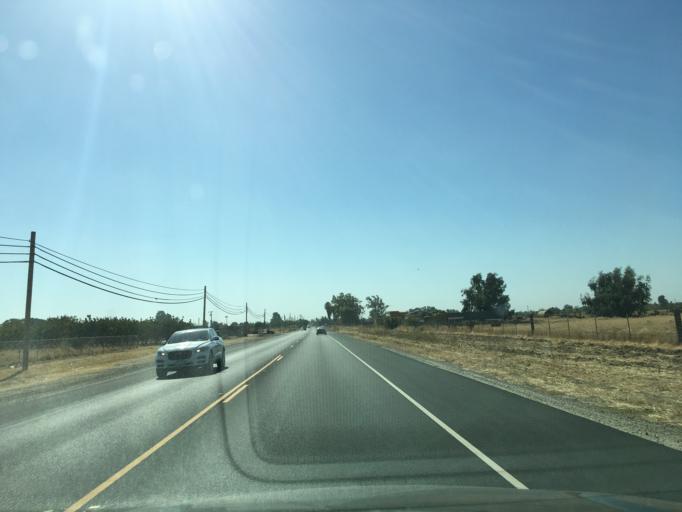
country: US
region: California
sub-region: Madera County
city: Parksdale
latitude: 36.9805
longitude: -120.0309
